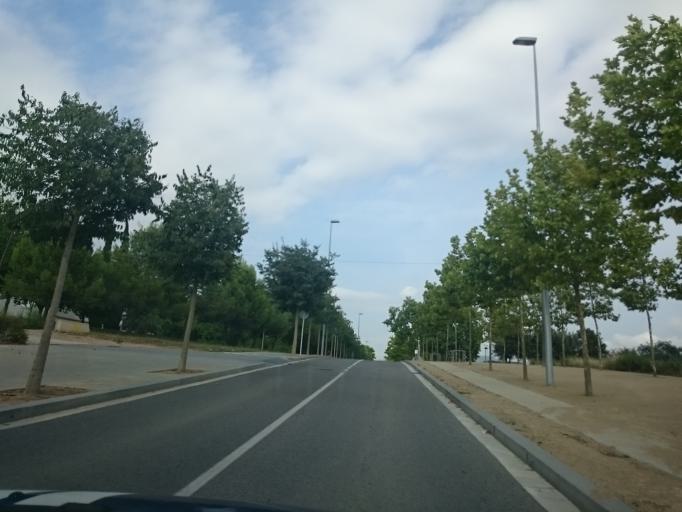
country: ES
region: Catalonia
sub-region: Provincia de Barcelona
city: Cerdanyola del Valles
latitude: 41.4866
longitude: 2.1228
